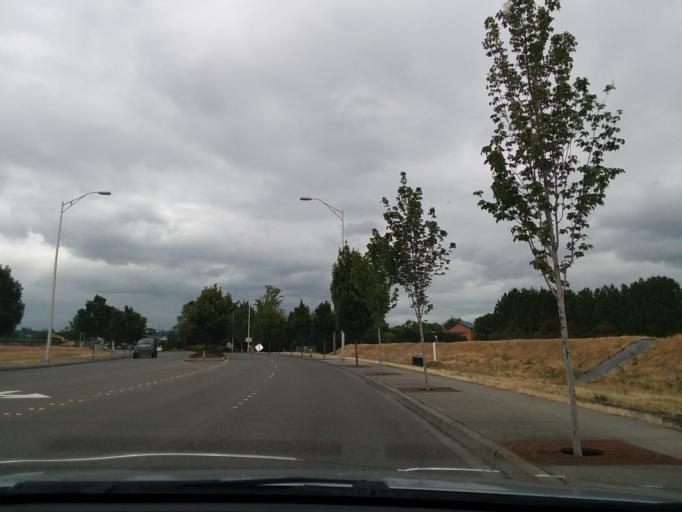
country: US
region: Washington
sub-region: King County
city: SeaTac
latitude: 47.4393
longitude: -122.2611
